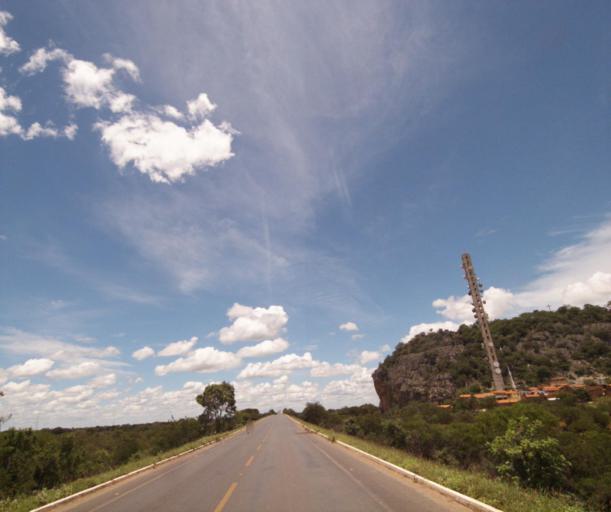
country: BR
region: Bahia
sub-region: Bom Jesus Da Lapa
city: Bom Jesus da Lapa
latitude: -13.2633
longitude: -43.4177
